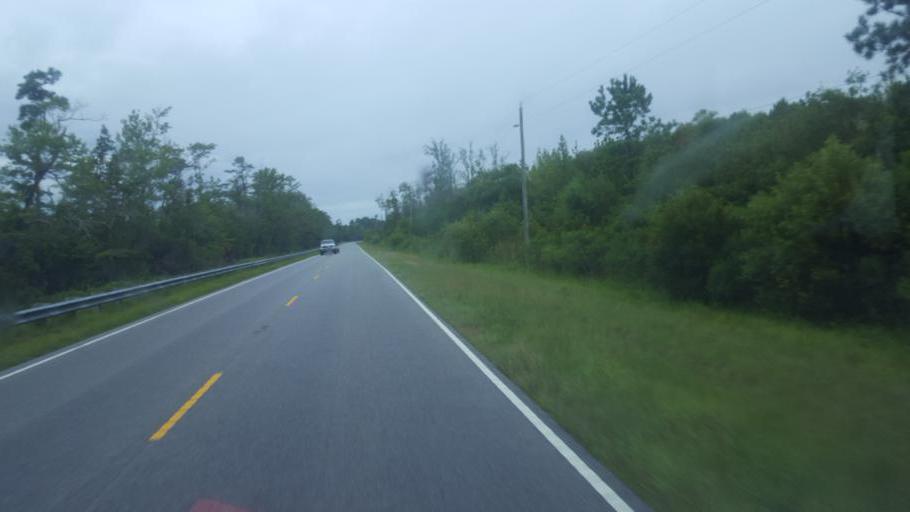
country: US
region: North Carolina
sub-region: Tyrrell County
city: Columbia
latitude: 35.9072
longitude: -76.1030
